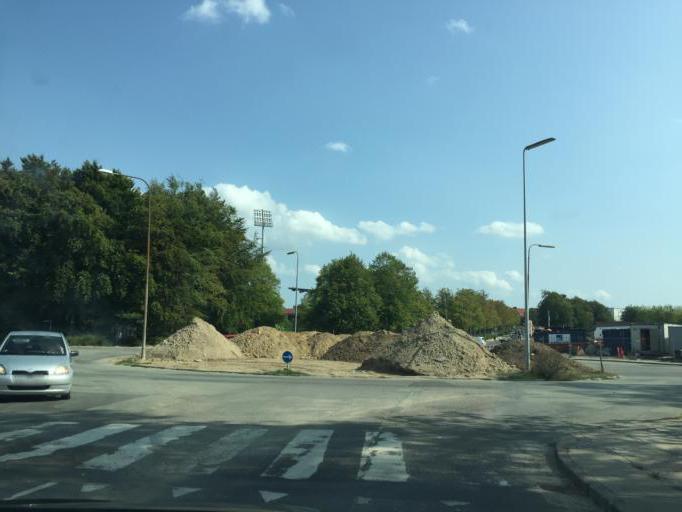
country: DK
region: South Denmark
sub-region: Odense Kommune
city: Odense
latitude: 55.3985
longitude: 10.3459
